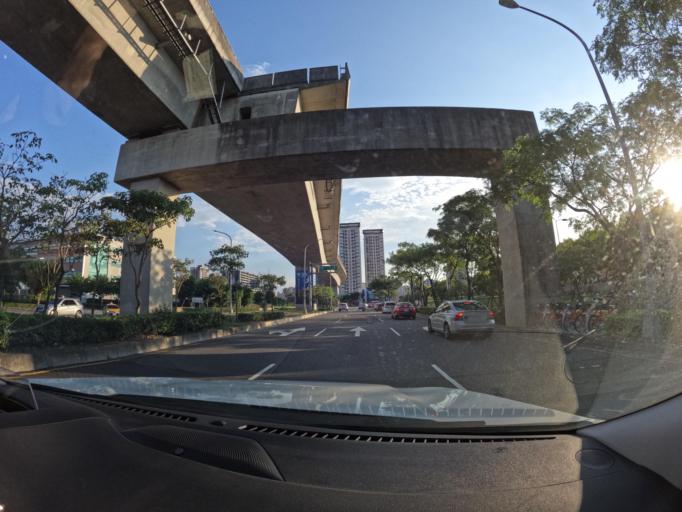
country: TW
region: Taiwan
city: Taoyuan City
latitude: 25.0129
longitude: 121.2132
